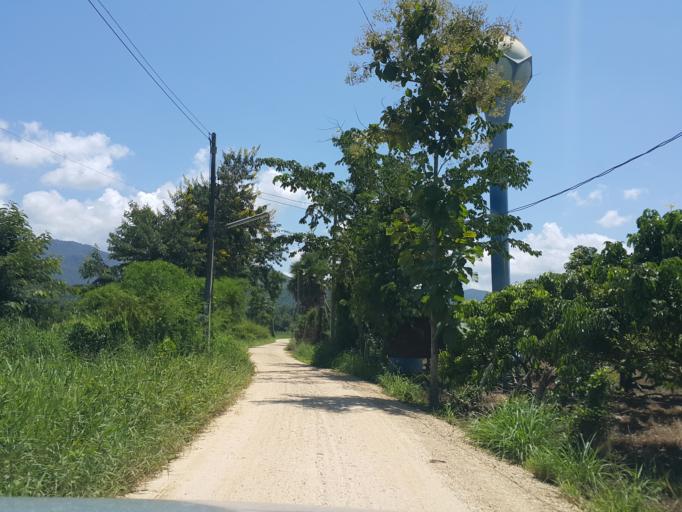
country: TH
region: Lamphun
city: Ban Thi
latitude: 18.6660
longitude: 99.1611
